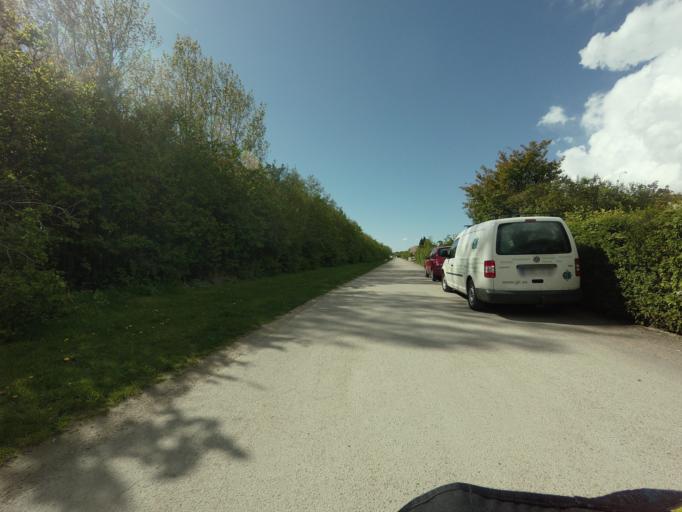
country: SE
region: Skane
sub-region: Landskrona
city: Landskrona
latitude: 55.8931
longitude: 12.8518
